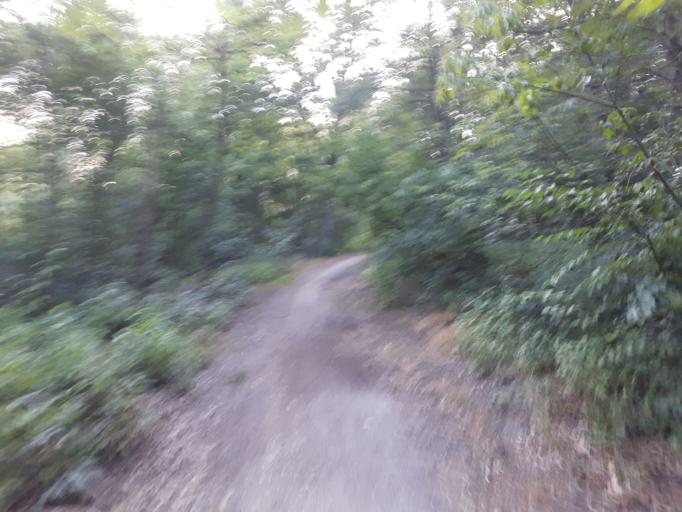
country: DE
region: Berlin
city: Staaken
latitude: 52.5551
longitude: 13.1320
